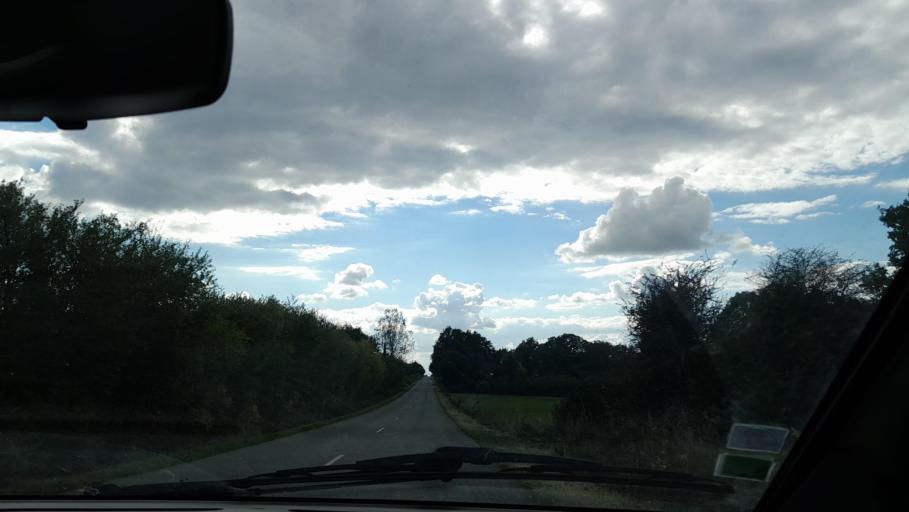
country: FR
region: Brittany
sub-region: Departement d'Ille-et-Vilaine
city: Le Pertre
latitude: 47.9792
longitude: -1.0145
